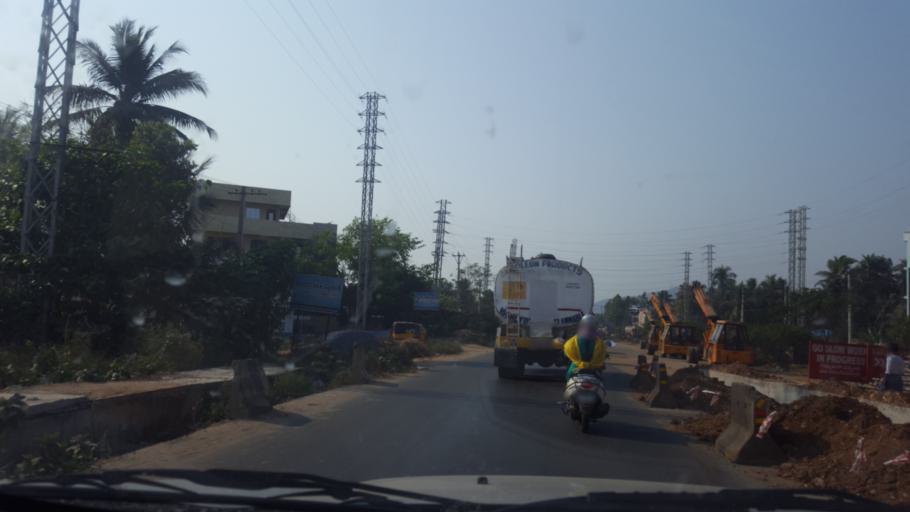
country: IN
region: Andhra Pradesh
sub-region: Vishakhapatnam
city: Anakapalle
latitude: 17.6753
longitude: 82.9970
